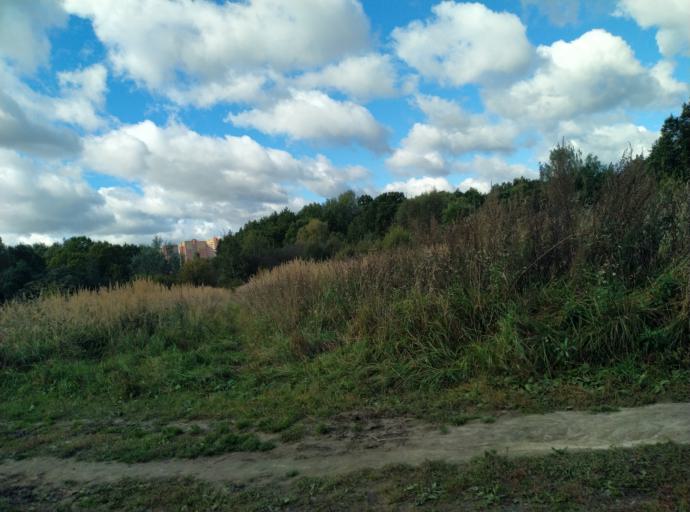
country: RU
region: Moscow
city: Khimki
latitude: 55.8630
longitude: 37.4111
